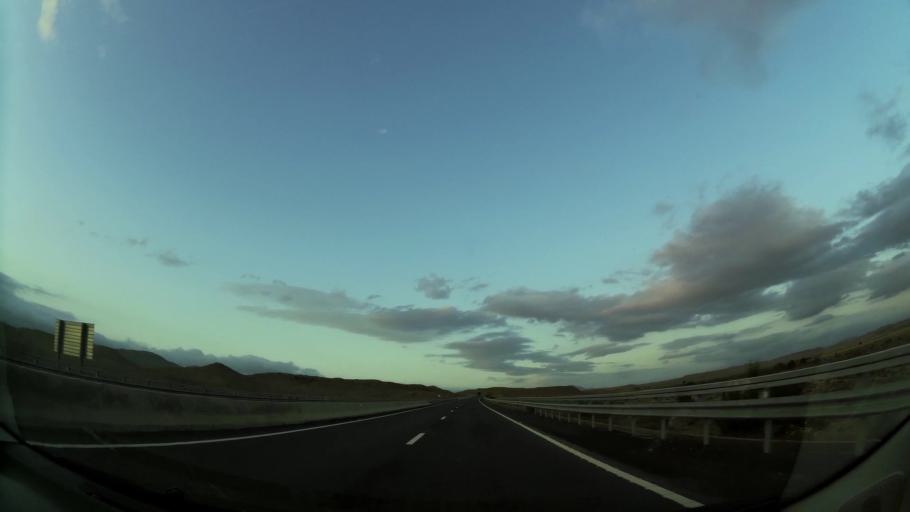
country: MA
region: Oriental
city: Taourirt
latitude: 34.5722
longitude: -2.8208
